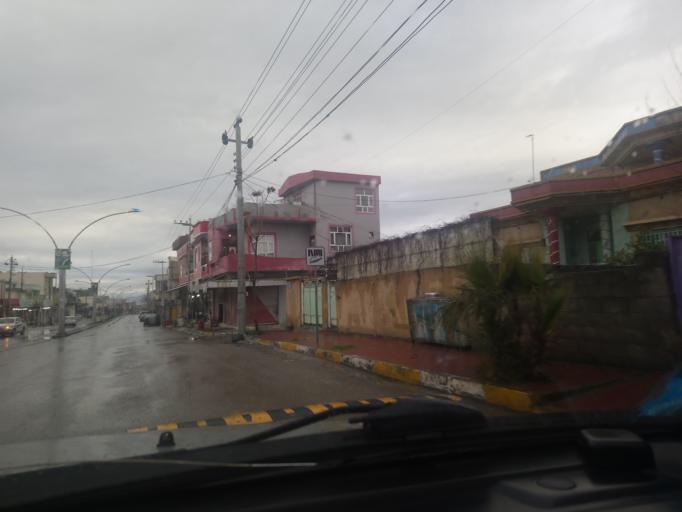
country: IQ
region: As Sulaymaniyah
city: Qeladize
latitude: 36.1782
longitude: 45.1398
